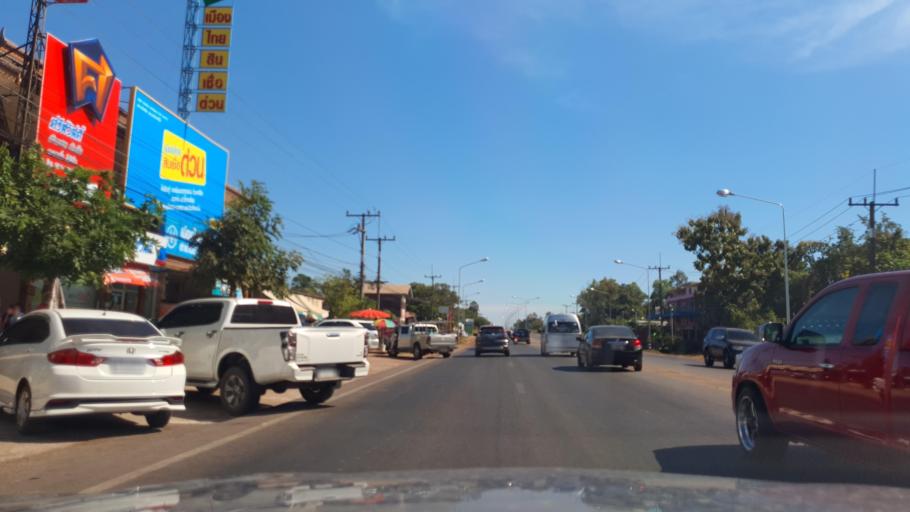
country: TH
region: Sakon Nakhon
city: Tao Ngoi
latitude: 17.0821
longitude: 104.1927
